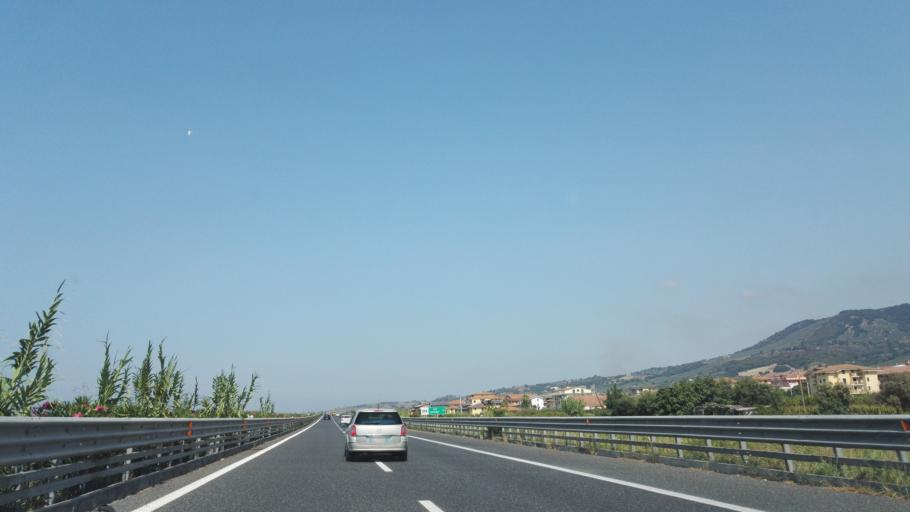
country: IT
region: Calabria
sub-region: Provincia di Catanzaro
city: Gizzeria
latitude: 38.9371
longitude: 16.2118
